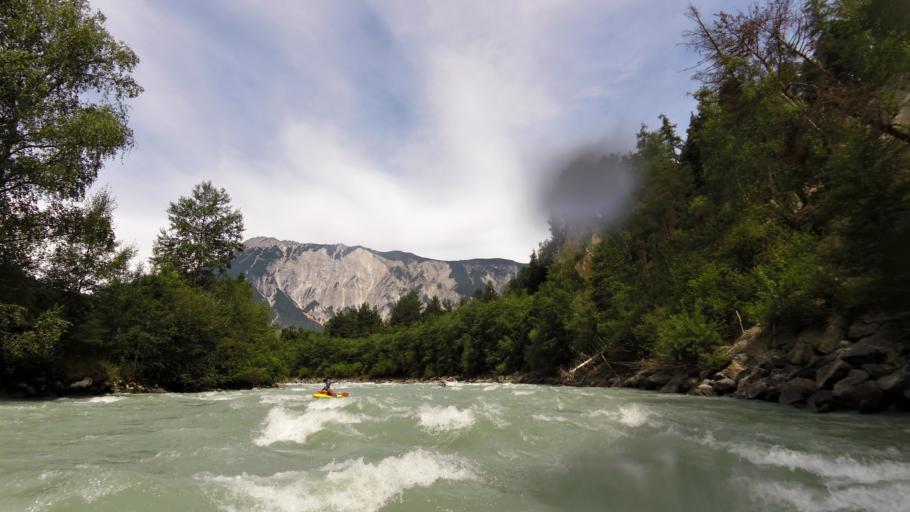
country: AT
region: Tyrol
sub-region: Politischer Bezirk Imst
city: Sautens
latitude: 47.2156
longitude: 10.8630
